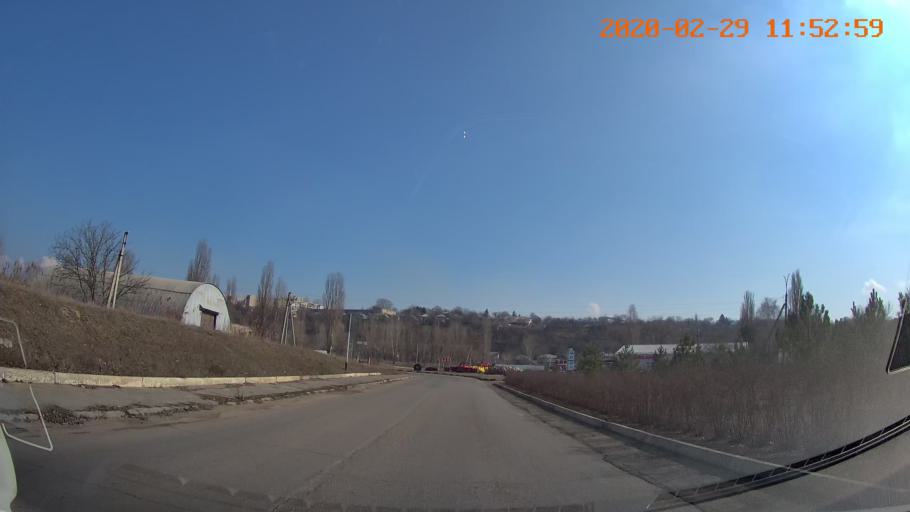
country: MD
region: Telenesti
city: Ribnita
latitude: 47.7750
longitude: 28.9888
